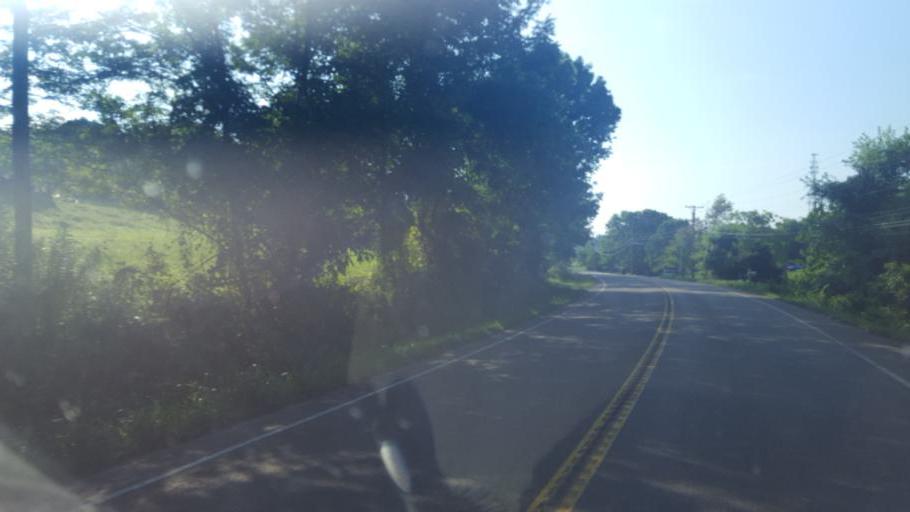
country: US
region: Tennessee
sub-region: Sullivan County
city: Blountville
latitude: 36.5591
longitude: -82.3435
